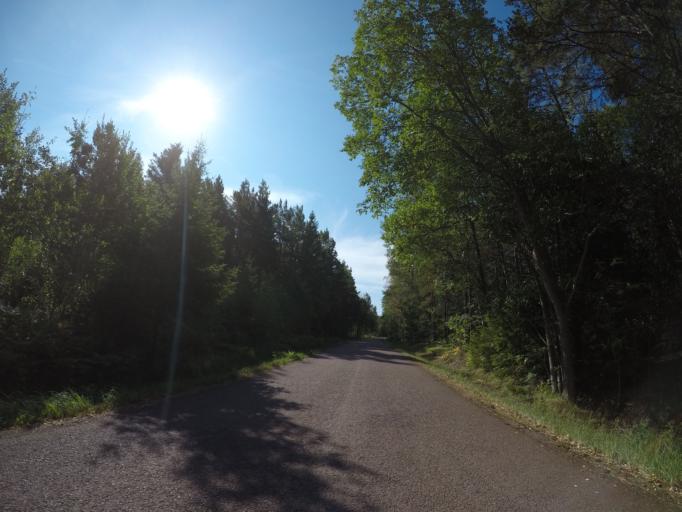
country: AX
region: Alands landsbygd
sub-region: Finstroem
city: Finstroem
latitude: 60.2774
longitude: 19.9175
